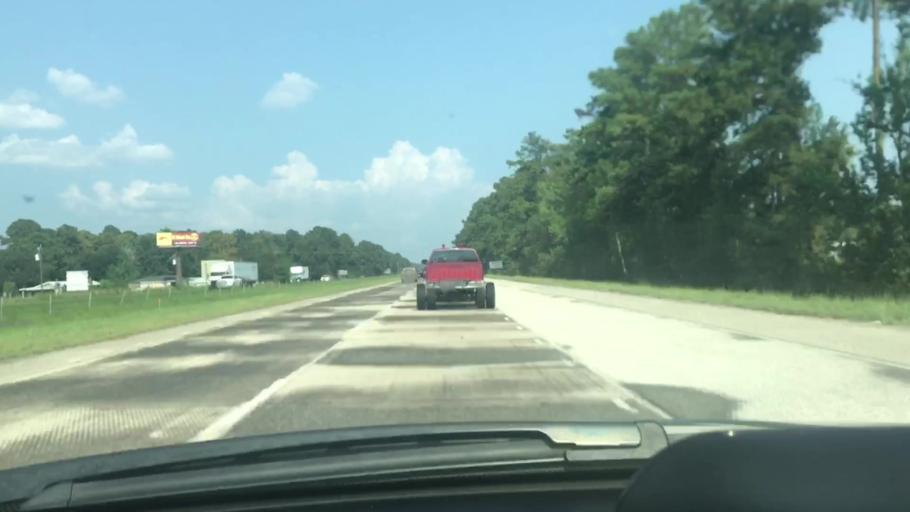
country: US
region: Louisiana
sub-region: Livingston Parish
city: Albany
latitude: 30.4792
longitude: -90.5367
